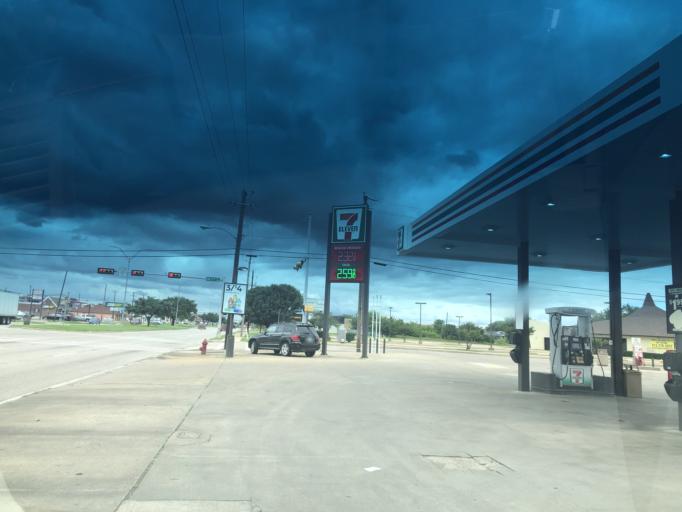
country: US
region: Texas
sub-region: Dallas County
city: Grand Prairie
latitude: 32.7097
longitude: -97.0070
